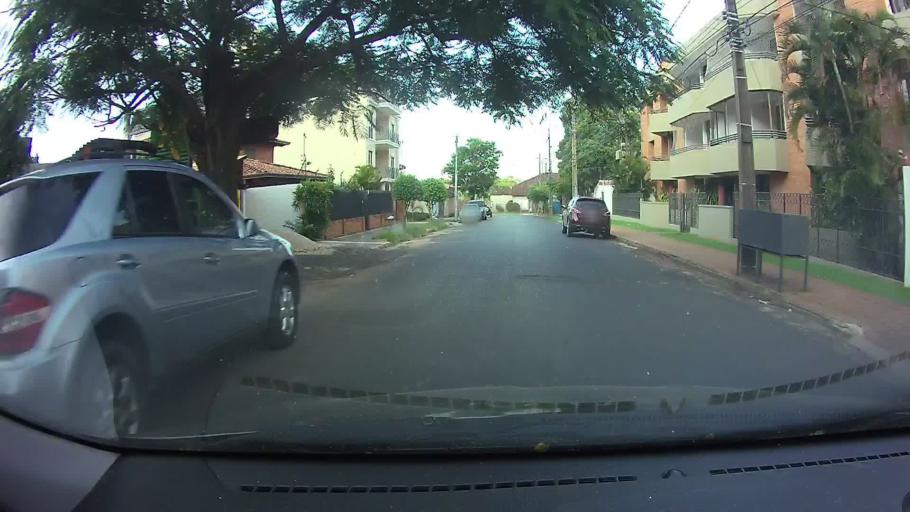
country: PY
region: Asuncion
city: Asuncion
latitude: -25.2783
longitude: -57.5737
